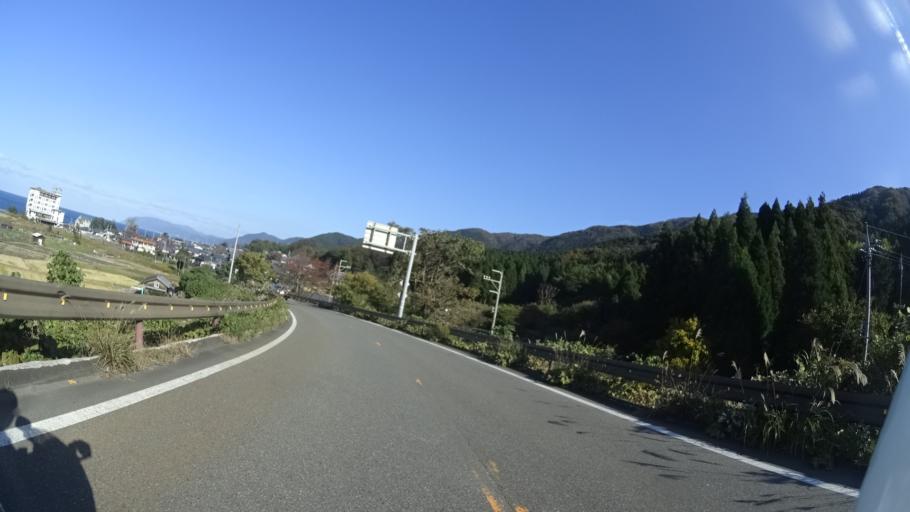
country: JP
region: Fukui
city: Tsuruga
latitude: 35.7445
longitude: 136.1029
